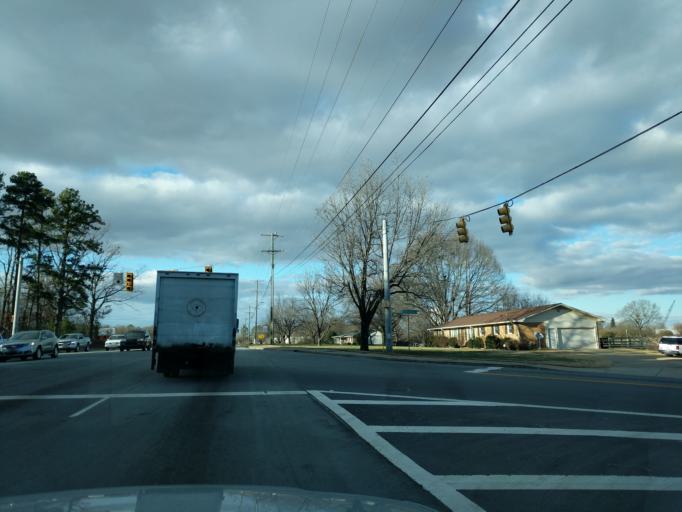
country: US
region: South Carolina
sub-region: Spartanburg County
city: Duncan
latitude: 34.8752
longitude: -82.1452
